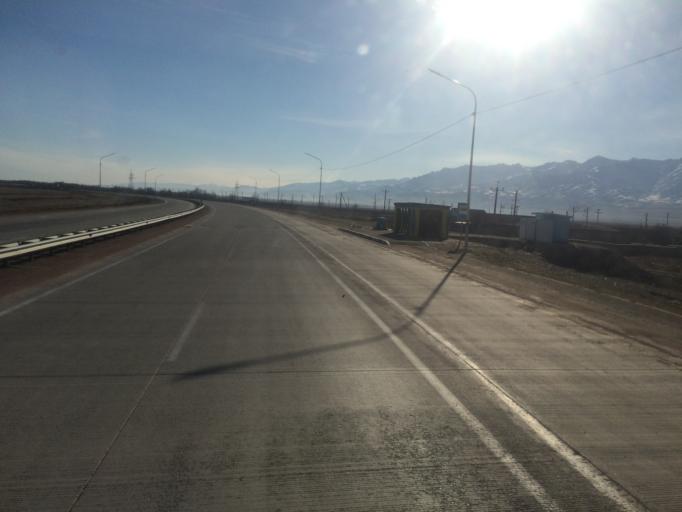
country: KG
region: Talas
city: Ivanovo-Alekseyevka
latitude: 42.9909
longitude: 72.1148
